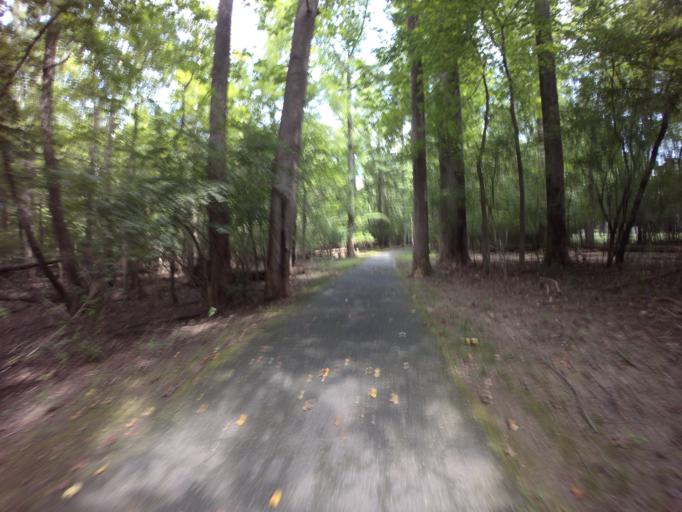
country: US
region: Maryland
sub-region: Montgomery County
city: South Kensington
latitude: 39.0232
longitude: -77.0982
